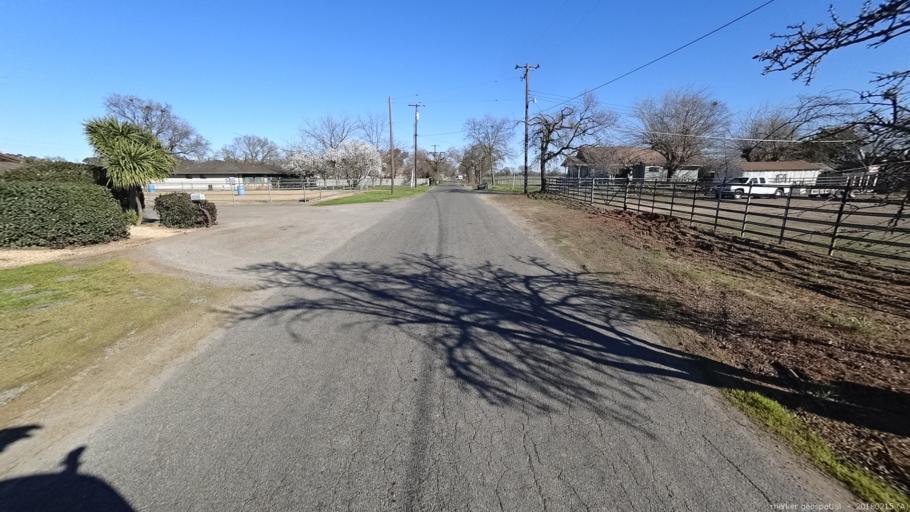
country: US
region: California
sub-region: Sacramento County
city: Rio Linda
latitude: 38.6695
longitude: -121.4638
